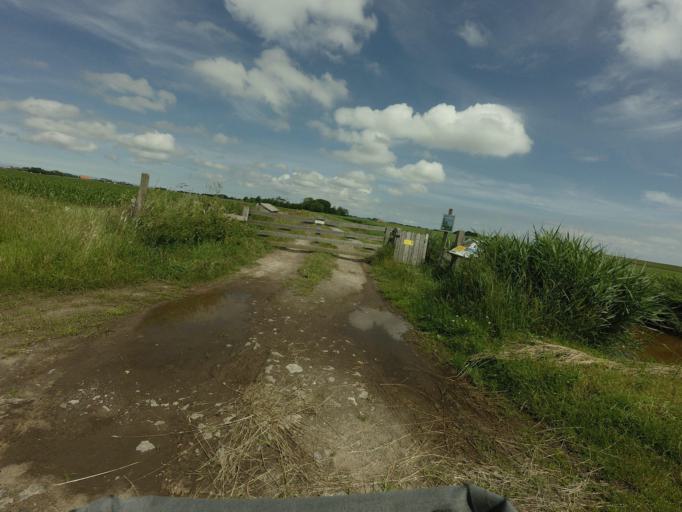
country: NL
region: North Holland
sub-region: Gemeente Texel
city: Den Burg
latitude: 53.0650
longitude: 4.8629
